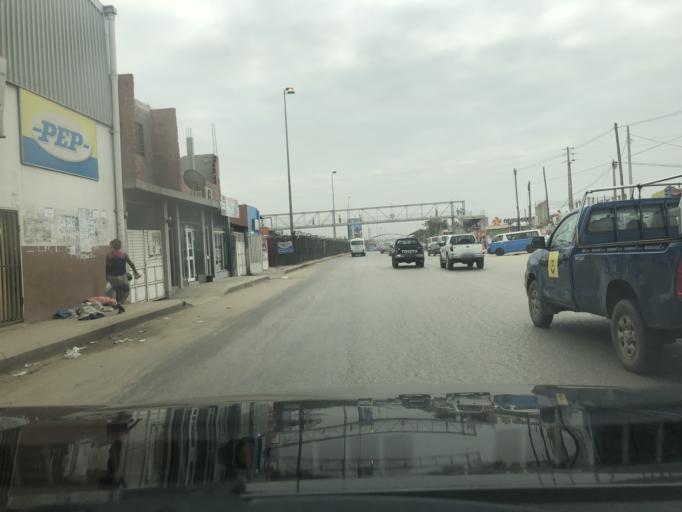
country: AO
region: Luanda
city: Luanda
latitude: -8.8830
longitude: 13.2521
